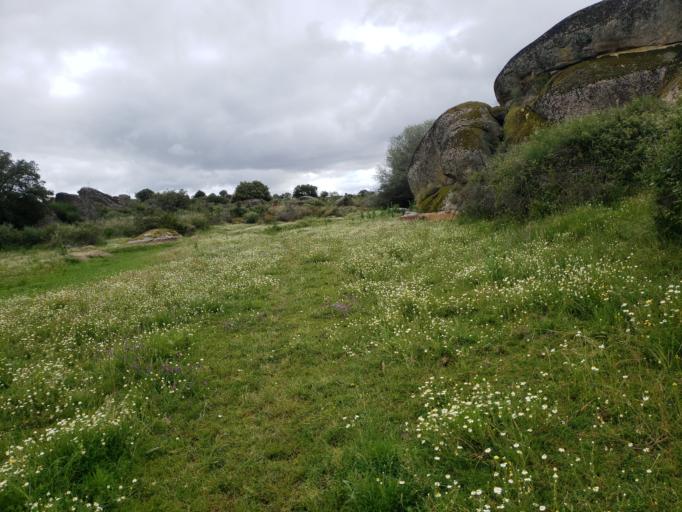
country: ES
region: Extremadura
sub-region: Provincia de Caceres
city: Malpartida de Caceres
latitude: 39.4244
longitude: -6.4951
